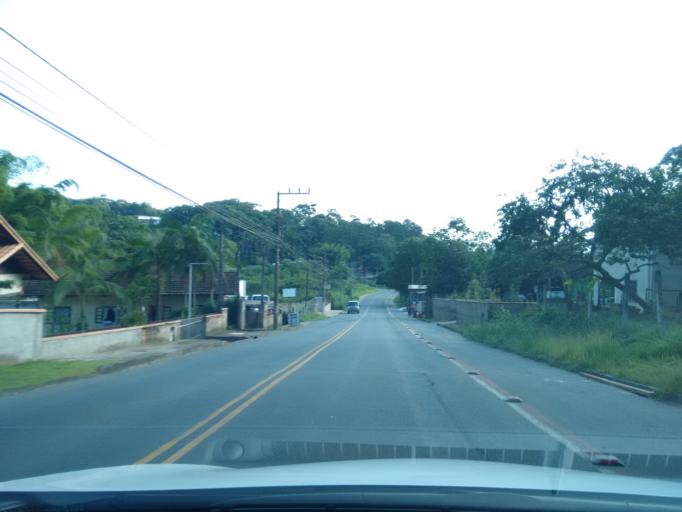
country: BR
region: Santa Catarina
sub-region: Blumenau
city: Blumenau
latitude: -26.8576
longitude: -49.0767
